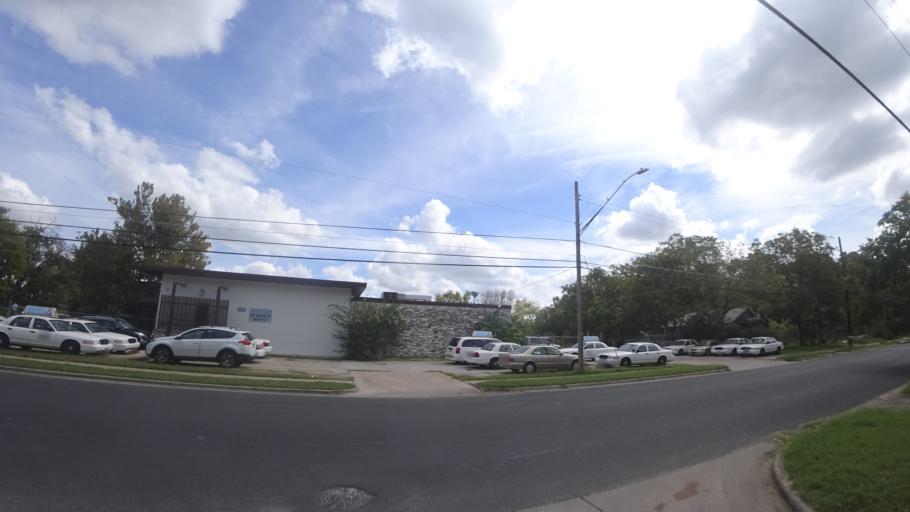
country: US
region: Texas
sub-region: Travis County
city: Austin
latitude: 30.2678
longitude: -97.6976
